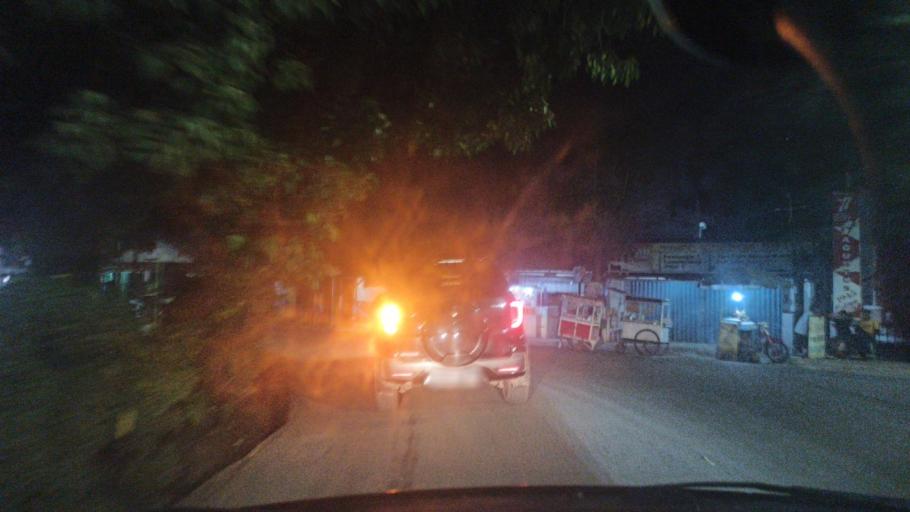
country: ID
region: South Sumatra
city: Palembang
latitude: -2.9220
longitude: 104.7800
